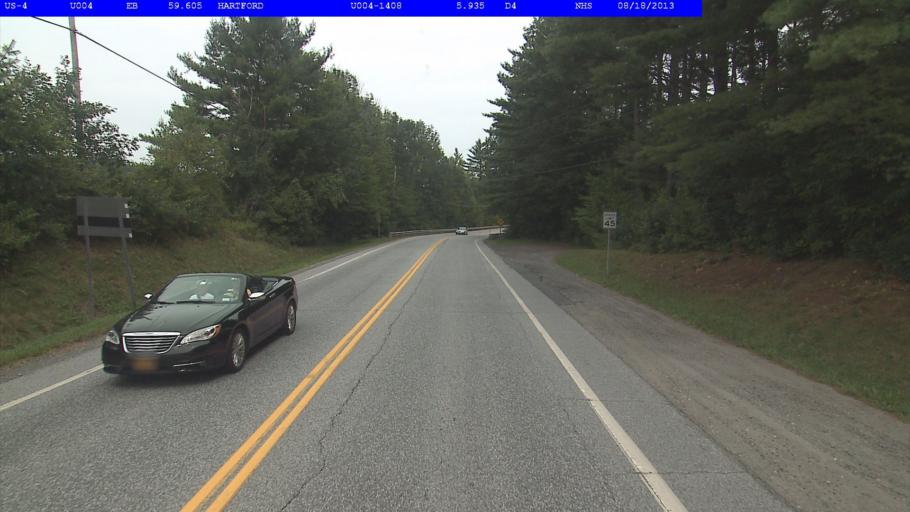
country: US
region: Vermont
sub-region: Windsor County
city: White River Junction
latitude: 43.6632
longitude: -72.3880
